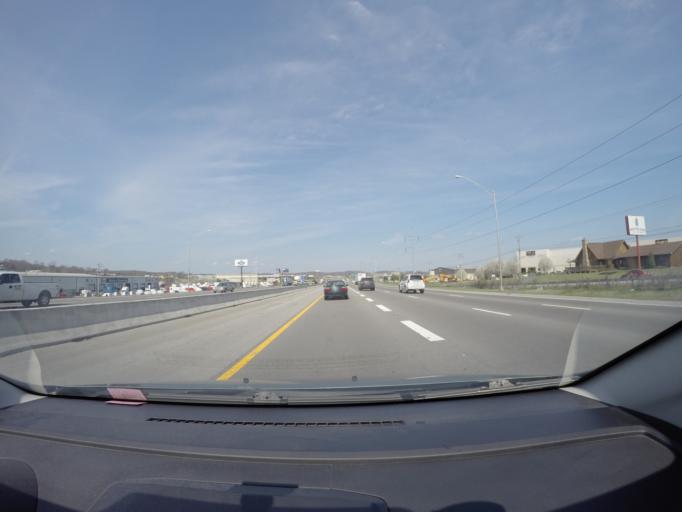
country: US
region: Tennessee
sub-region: Rutherford County
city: La Vergne
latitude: 35.9909
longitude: -86.5895
